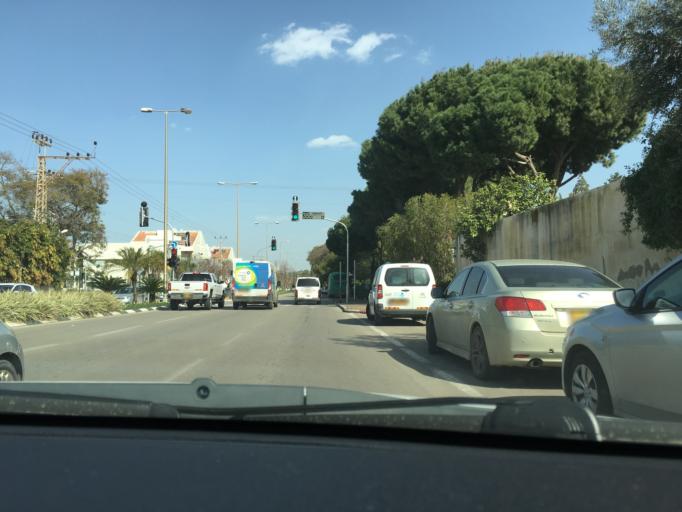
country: IL
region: Central District
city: Kfar Saba
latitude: 32.1839
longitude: 34.9009
